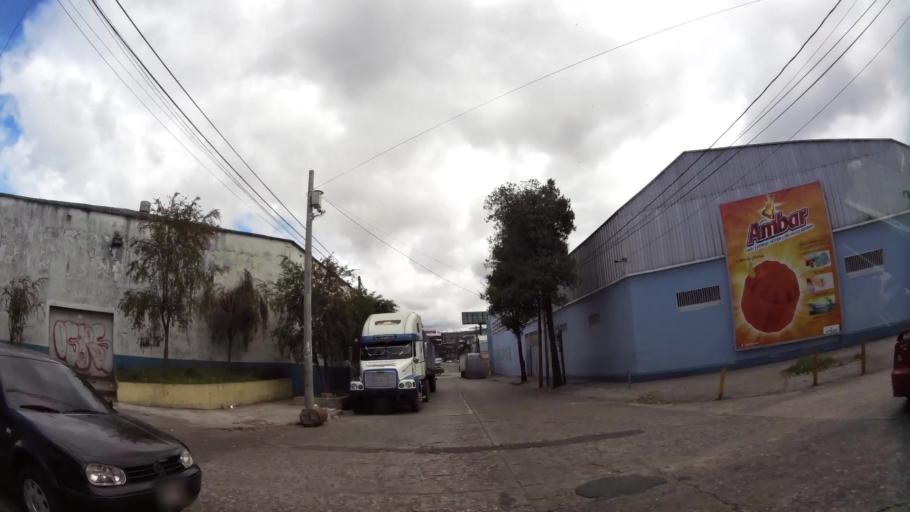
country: GT
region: Guatemala
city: Guatemala City
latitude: 14.6209
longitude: -90.5186
